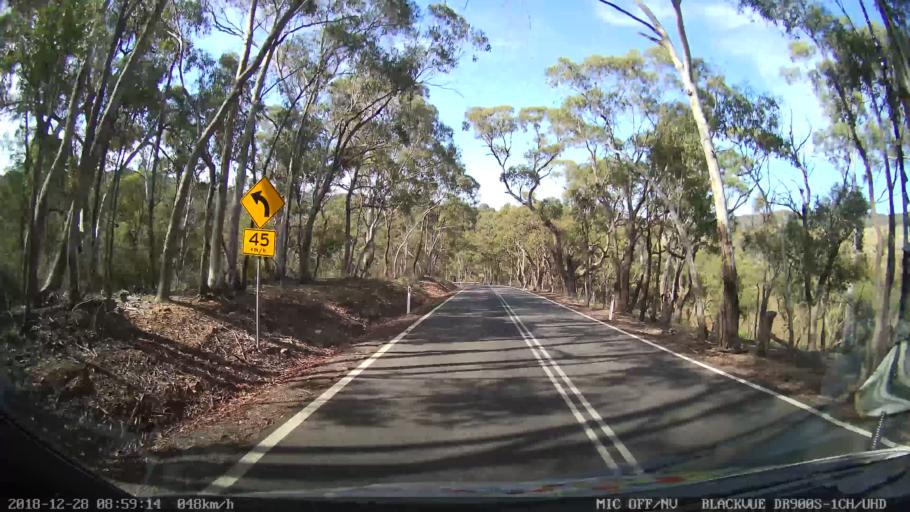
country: AU
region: New South Wales
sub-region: Upper Lachlan Shire
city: Crookwell
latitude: -34.1326
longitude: 149.3320
